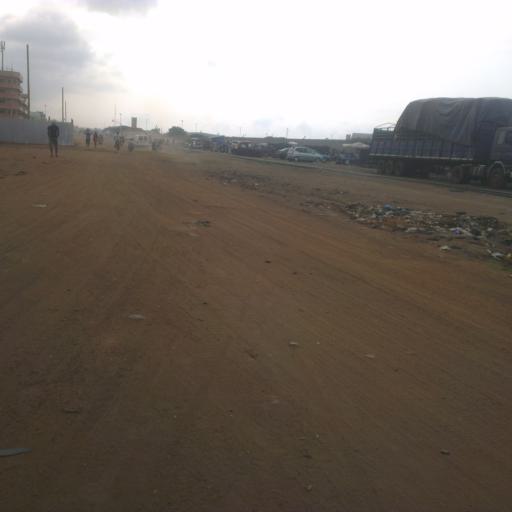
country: TG
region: Maritime
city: Lome
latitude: 6.1581
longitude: 1.2821
